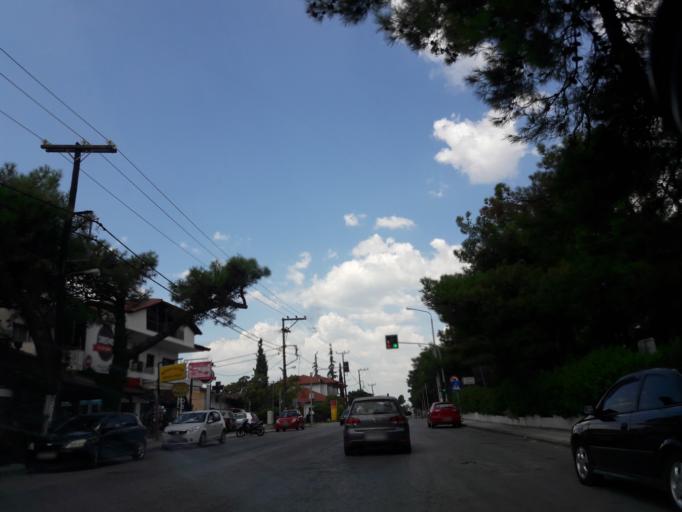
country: GR
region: Central Macedonia
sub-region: Nomos Thessalonikis
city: Thermi
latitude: 40.5242
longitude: 23.0505
